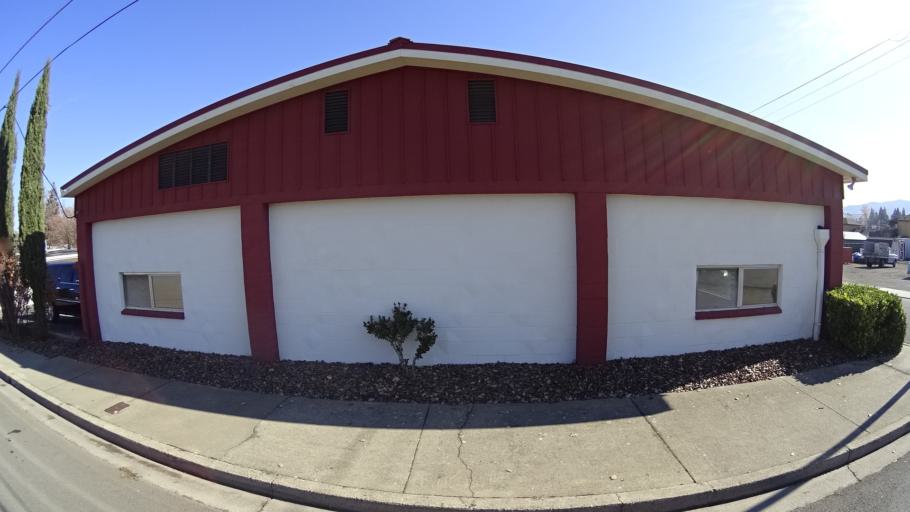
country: US
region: California
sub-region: Siskiyou County
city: Yreka
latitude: 41.7223
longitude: -122.6407
